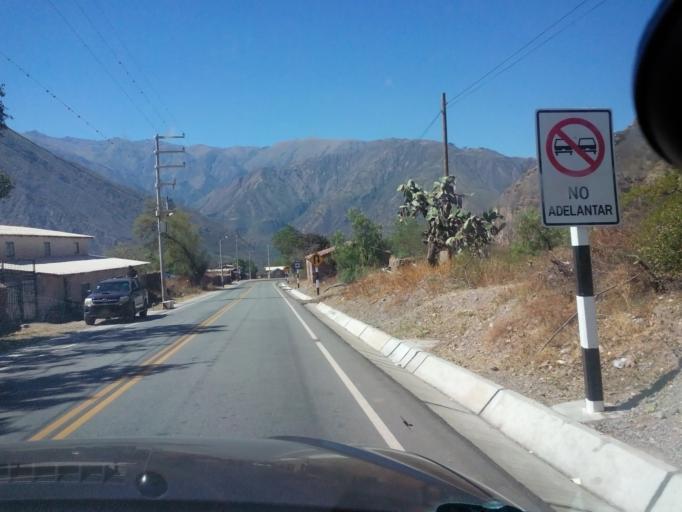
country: PE
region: Ayacucho
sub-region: Provincia de Huamanga
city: Ocros
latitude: -13.4228
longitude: -73.8531
